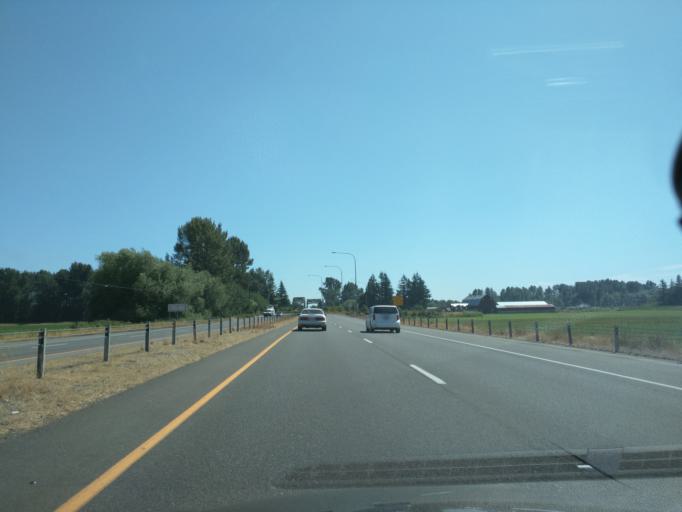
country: US
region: Washington
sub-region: Whatcom County
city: Lynden
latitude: 48.9254
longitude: -122.4857
